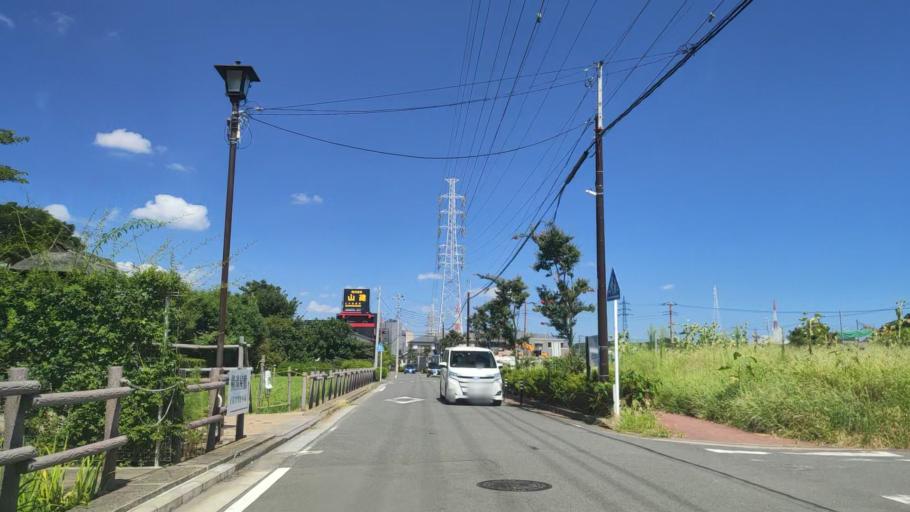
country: JP
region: Kanagawa
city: Yokohama
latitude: 35.5212
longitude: 139.6427
